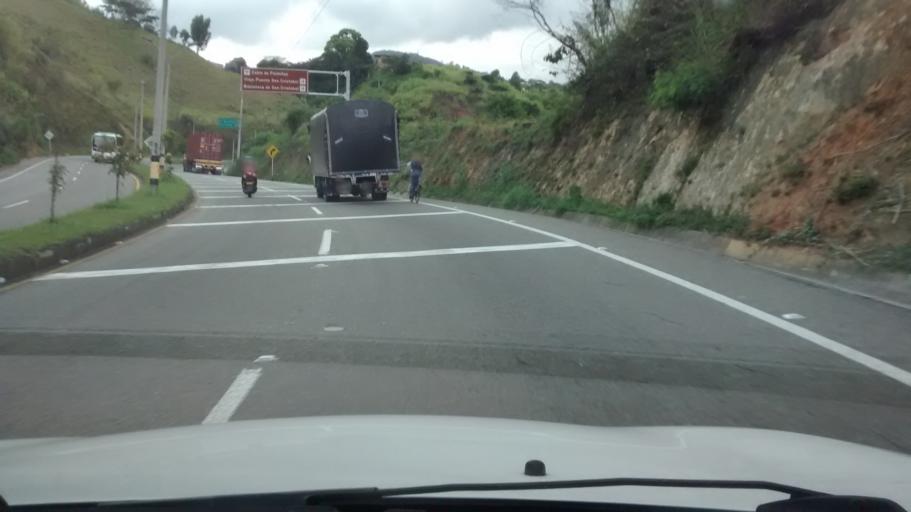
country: CO
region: Antioquia
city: Medellin
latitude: 6.2763
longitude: -75.6280
